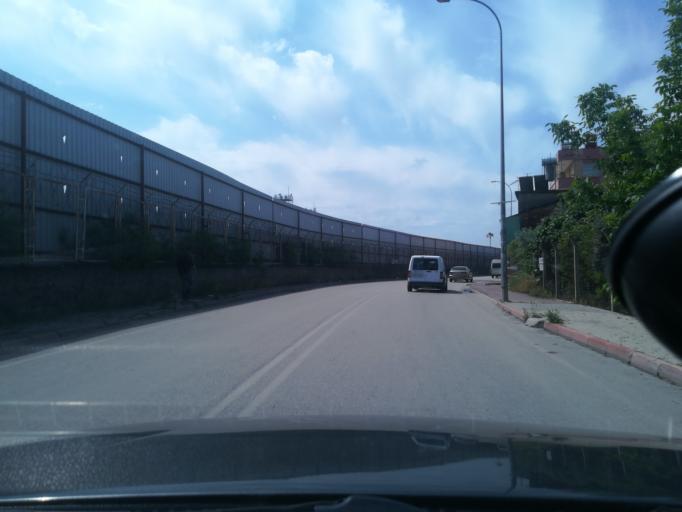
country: TR
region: Adana
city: Seyhan
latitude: 36.9914
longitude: 35.2875
